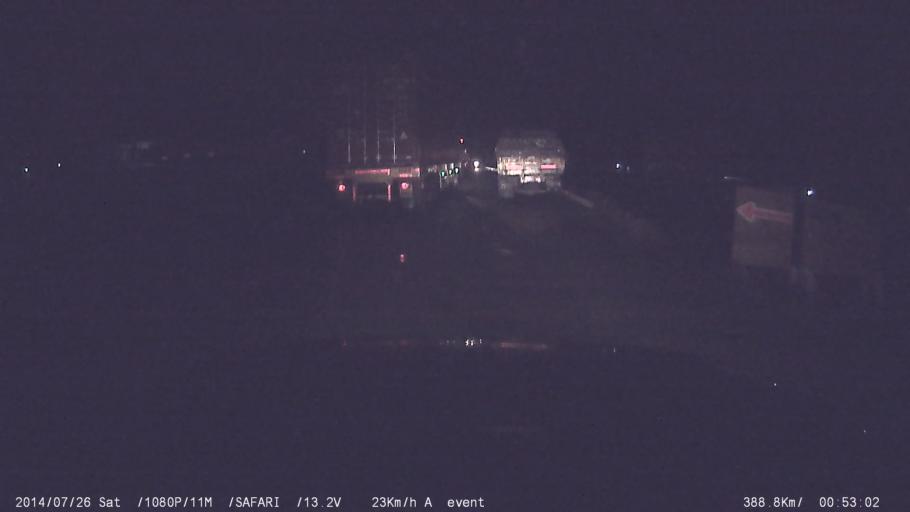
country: IN
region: Kerala
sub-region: Palakkad district
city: Palakkad
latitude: 10.7973
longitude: 76.7421
